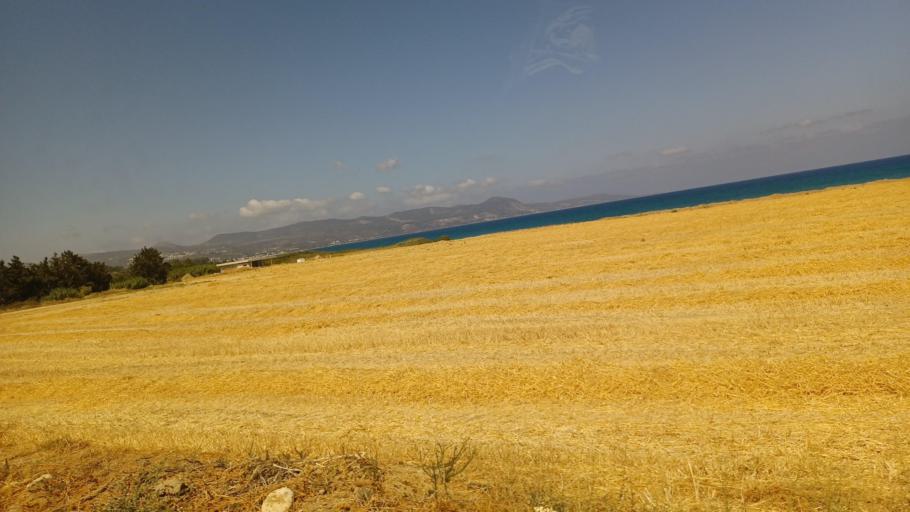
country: CY
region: Pafos
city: Polis
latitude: 35.0482
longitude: 32.4400
